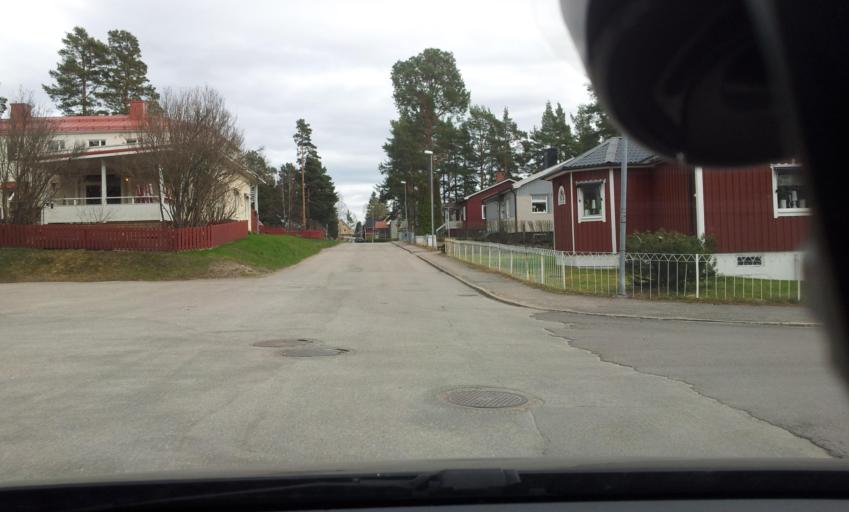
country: SE
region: Gaevleborg
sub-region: Ljusdals Kommun
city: Ljusdal
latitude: 61.8286
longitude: 16.1079
